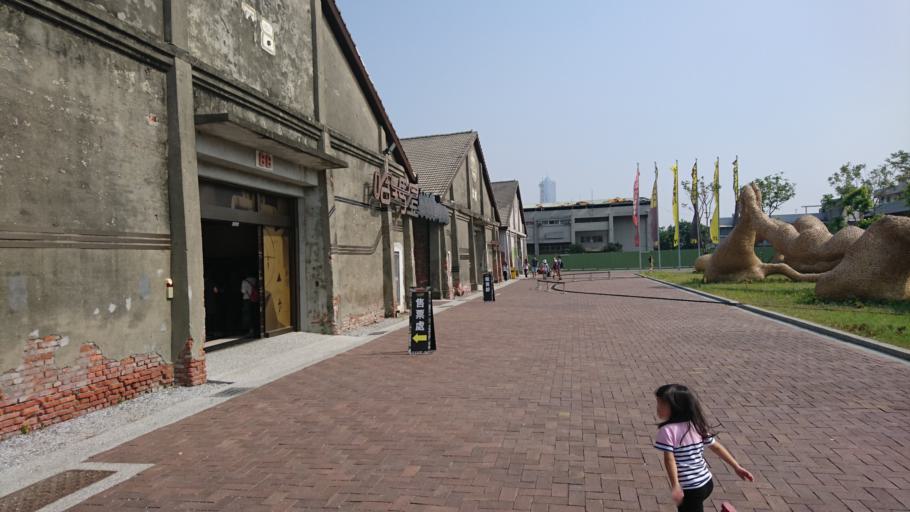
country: TW
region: Kaohsiung
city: Kaohsiung
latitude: 22.6206
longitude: 120.2782
